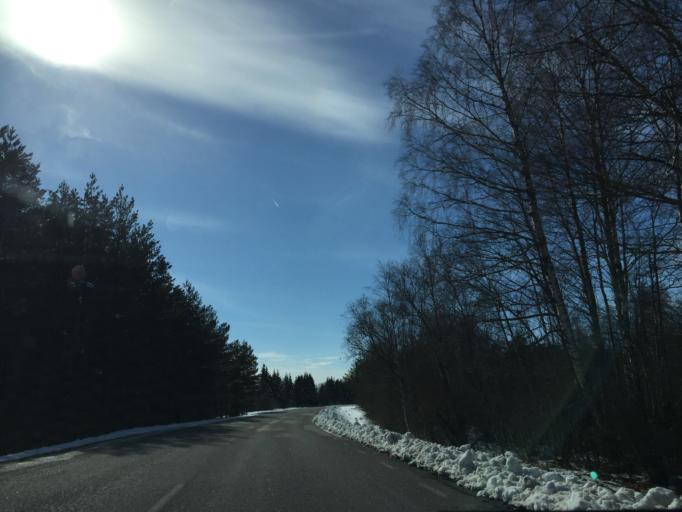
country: EE
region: Saare
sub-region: Orissaare vald
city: Orissaare
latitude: 58.4010
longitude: 22.9918
